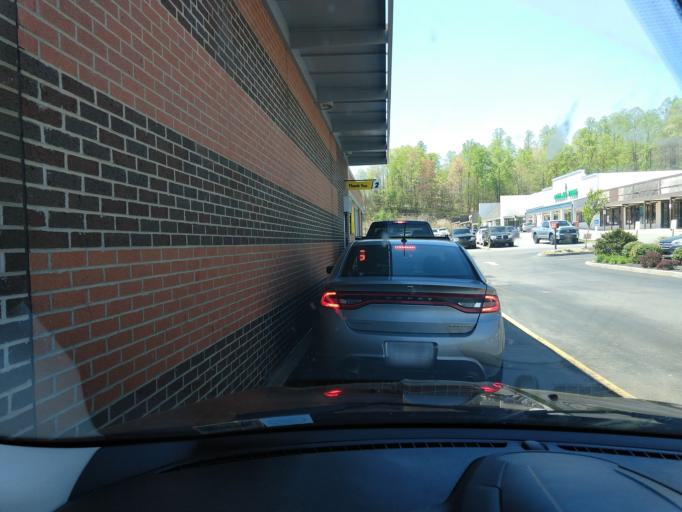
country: US
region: West Virginia
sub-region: Raleigh County
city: Crab Orchard
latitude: 37.7281
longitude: -81.2437
